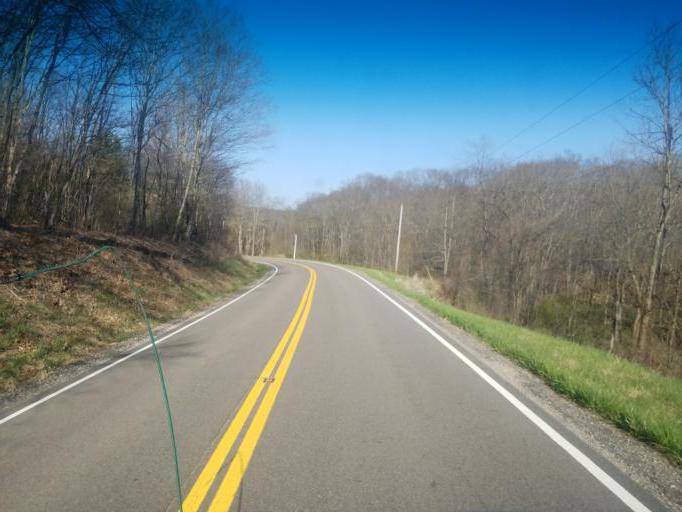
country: US
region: Ohio
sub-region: Muskingum County
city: Frazeysburg
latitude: 40.2768
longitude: -82.1035
